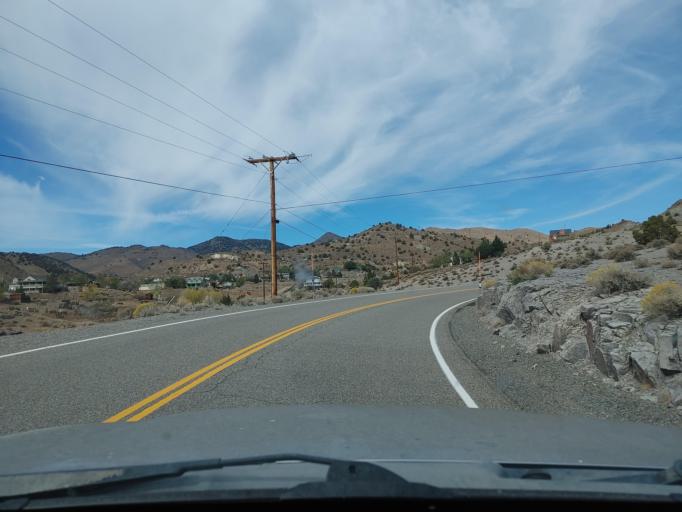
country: US
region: Nevada
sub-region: Storey County
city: Virginia City
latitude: 39.2619
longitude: -119.6360
